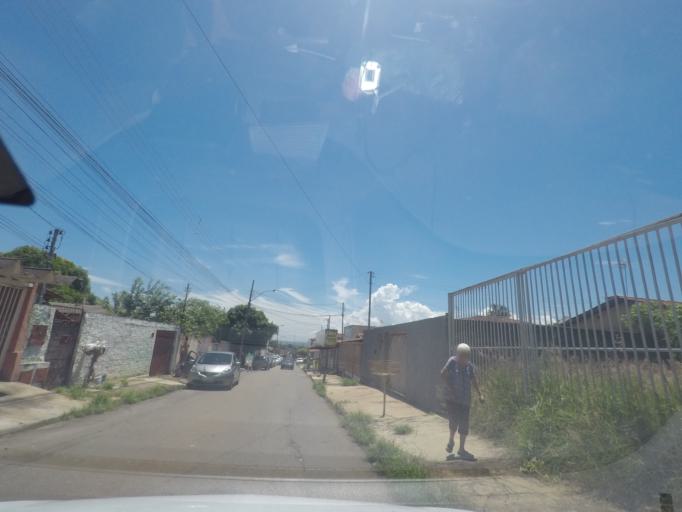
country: BR
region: Goias
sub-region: Aparecida De Goiania
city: Aparecida de Goiania
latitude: -16.7670
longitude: -49.3454
